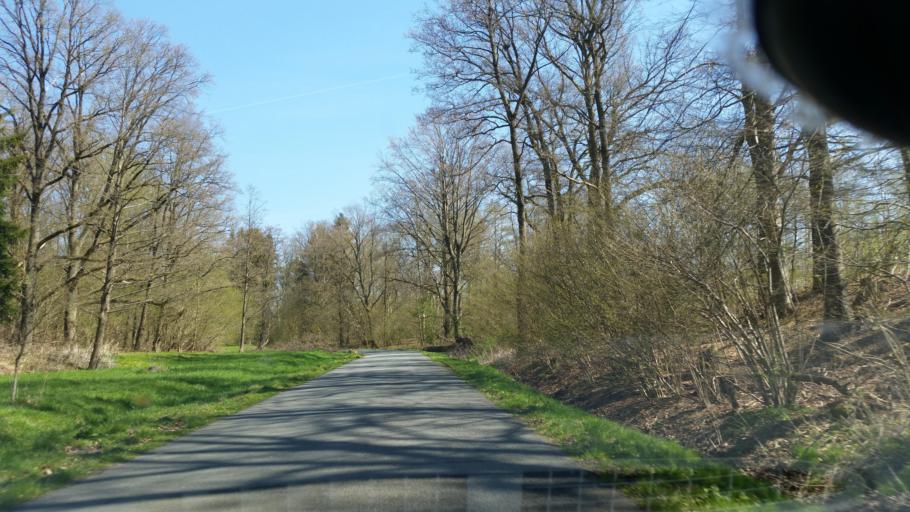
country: DE
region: Lower Saxony
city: Bad Fallingbostel
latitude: 52.8543
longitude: 9.7319
